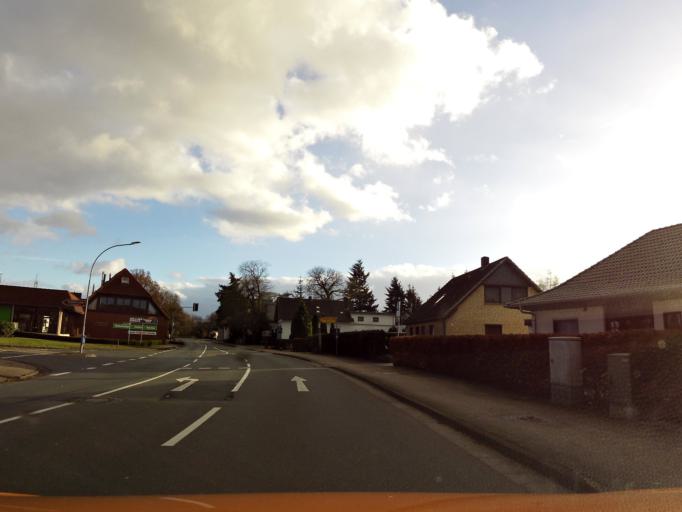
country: DE
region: Lower Saxony
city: Langwedel
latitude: 52.9733
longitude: 9.1965
